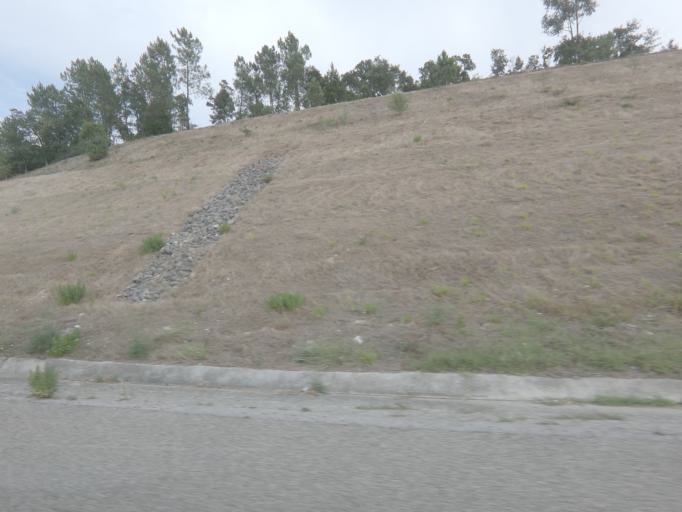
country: PT
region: Coimbra
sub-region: Coimbra
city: Coimbra
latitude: 40.2029
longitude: -8.4524
